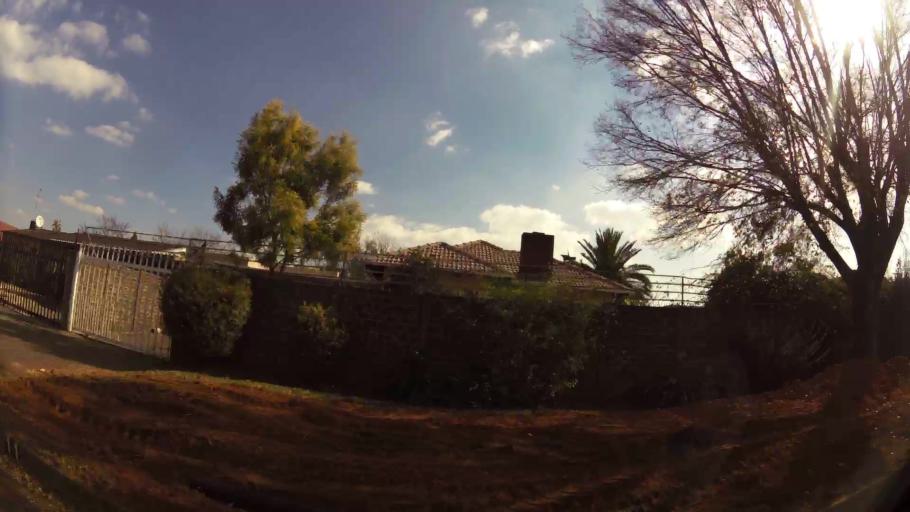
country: ZA
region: Gauteng
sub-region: Ekurhuleni Metropolitan Municipality
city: Germiston
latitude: -26.1834
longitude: 28.1982
